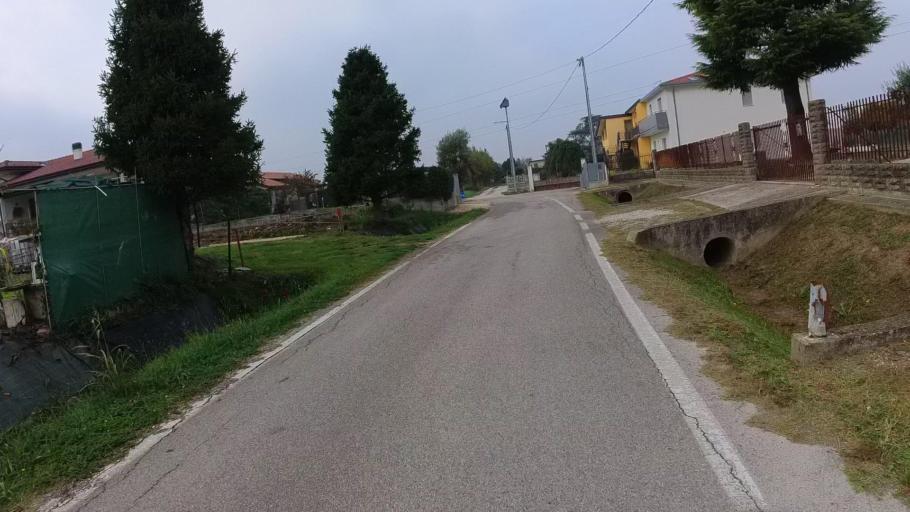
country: IT
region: Veneto
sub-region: Provincia di Venezia
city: Fosso
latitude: 45.3875
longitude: 12.0374
